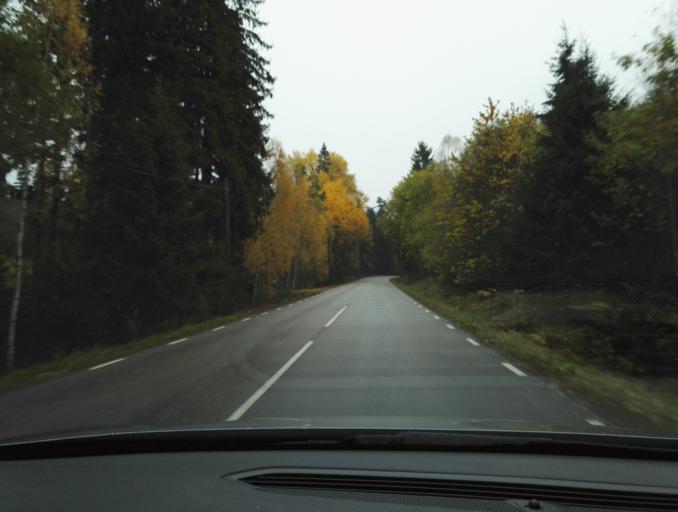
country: SE
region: Kronoberg
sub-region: Vaxjo Kommun
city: Rottne
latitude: 57.0279
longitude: 14.8244
